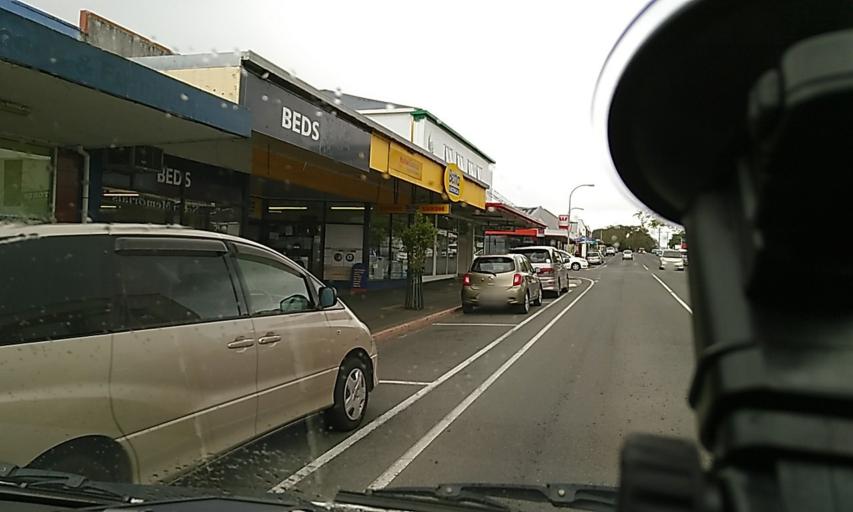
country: NZ
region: Northland
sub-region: Far North District
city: Waimate North
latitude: -35.4082
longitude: 173.7988
